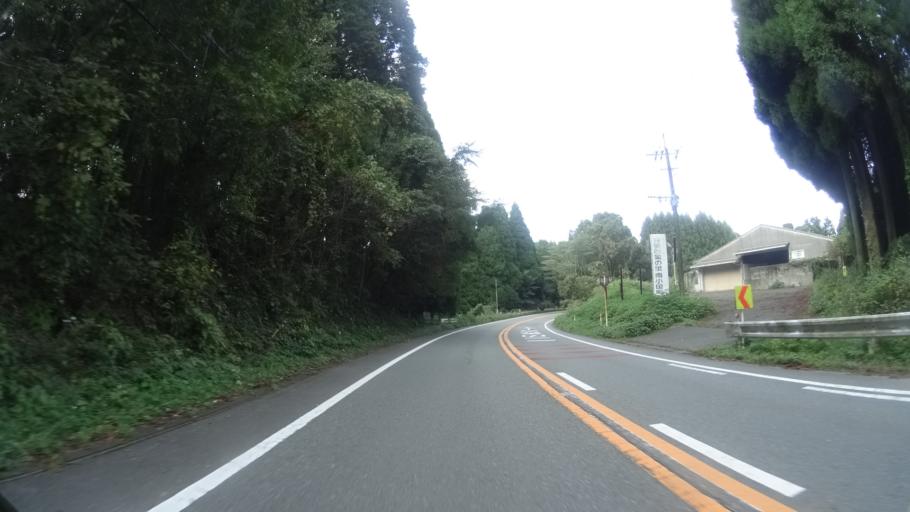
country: JP
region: Kumamoto
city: Aso
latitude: 33.0625
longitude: 131.0671
